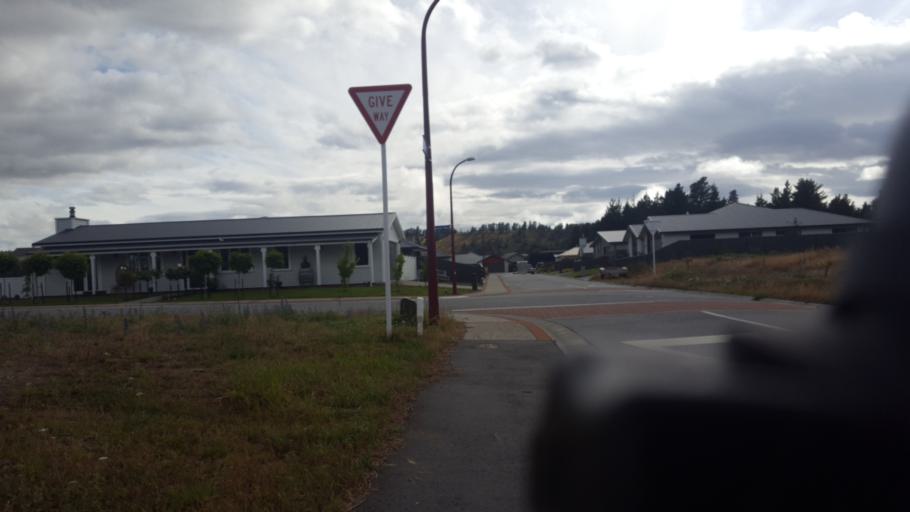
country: NZ
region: Otago
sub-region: Queenstown-Lakes District
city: Wanaka
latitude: -45.2420
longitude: 169.3788
